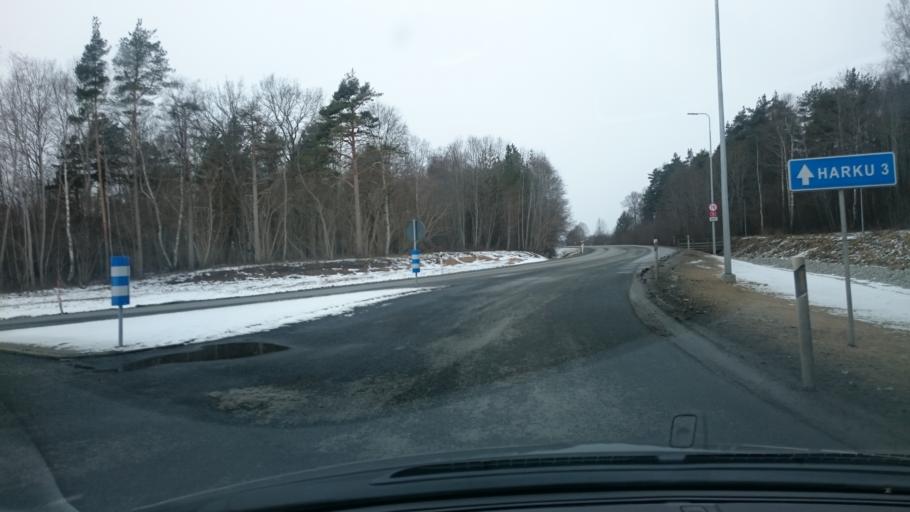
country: EE
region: Harju
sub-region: Saue vald
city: Laagri
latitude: 59.3612
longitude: 24.6000
